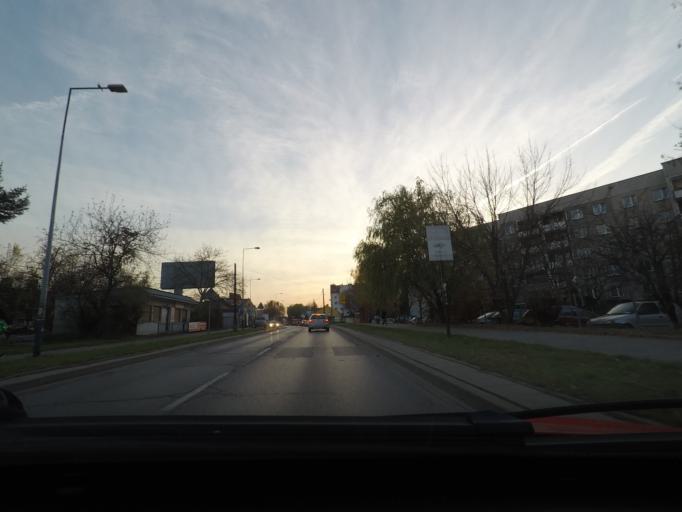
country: PL
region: Lesser Poland Voivodeship
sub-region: Krakow
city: Krakow
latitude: 50.0248
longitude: 19.9118
